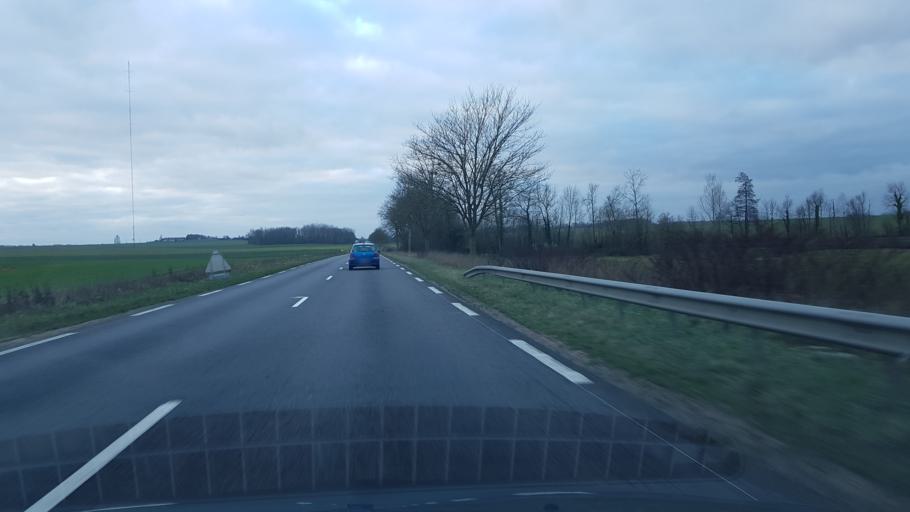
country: FR
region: Champagne-Ardenne
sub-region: Departement de la Marne
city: Esternay
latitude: 48.7174
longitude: 3.5158
